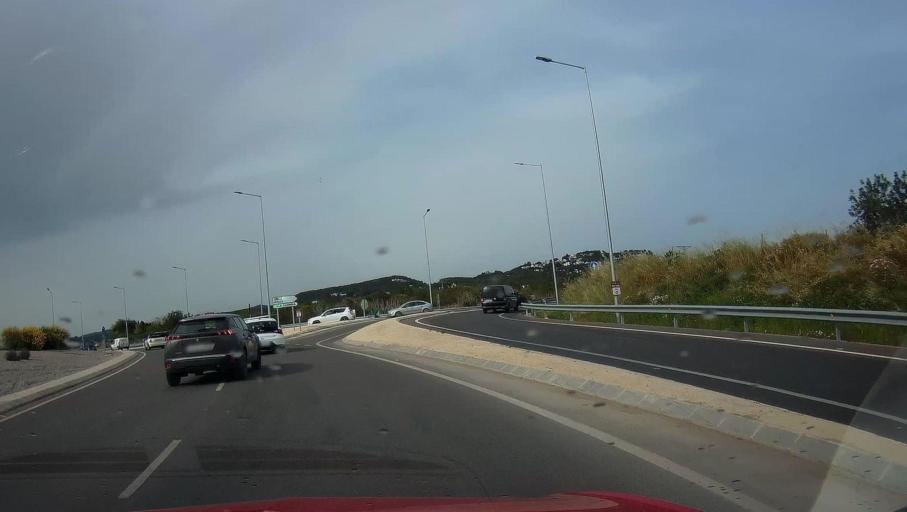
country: ES
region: Balearic Islands
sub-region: Illes Balears
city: Ibiza
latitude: 38.9353
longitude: 1.4446
